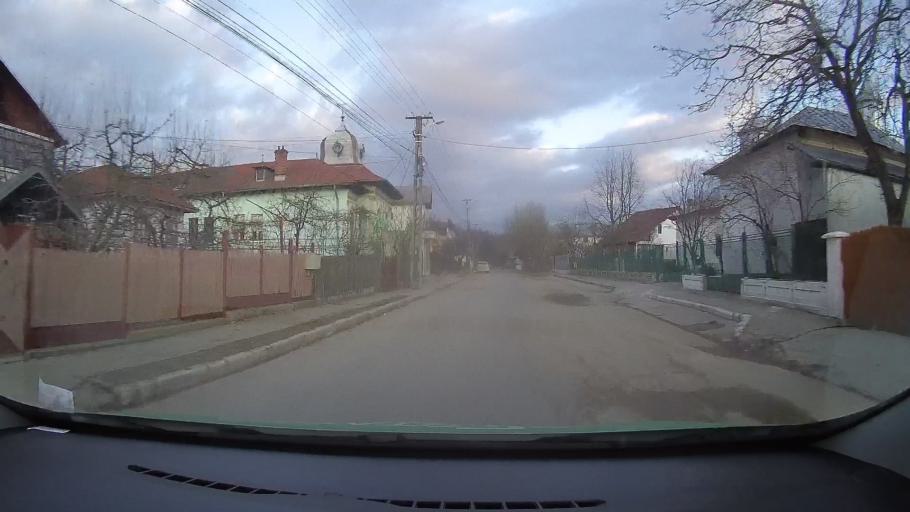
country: RO
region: Dambovita
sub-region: Municipiul Moreni
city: Moreni
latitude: 44.9928
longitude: 25.6432
